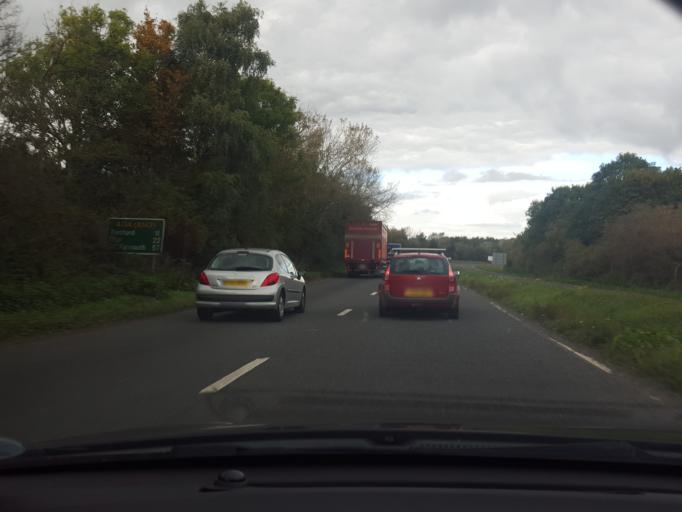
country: GB
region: England
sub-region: Suffolk
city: Bury St Edmunds
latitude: 52.2577
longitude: 0.7187
